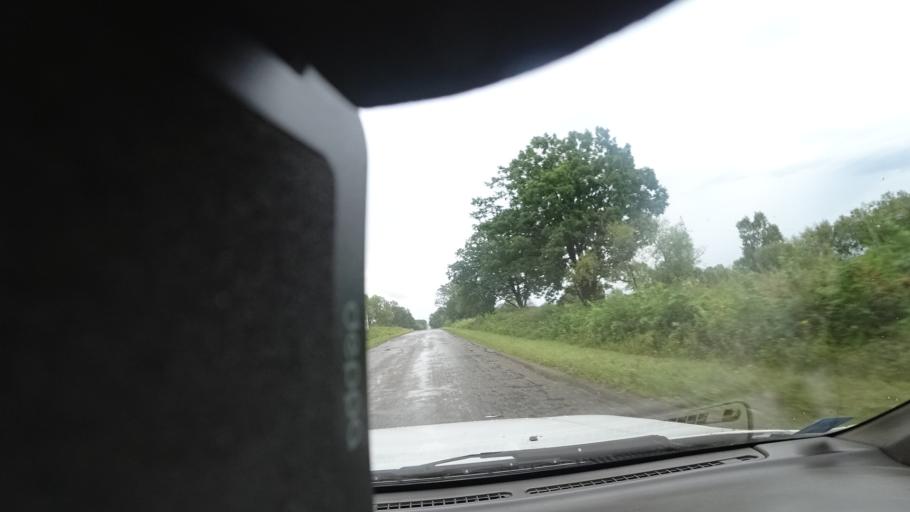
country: RU
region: Primorskiy
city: Lazo
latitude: 45.8700
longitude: 133.6947
